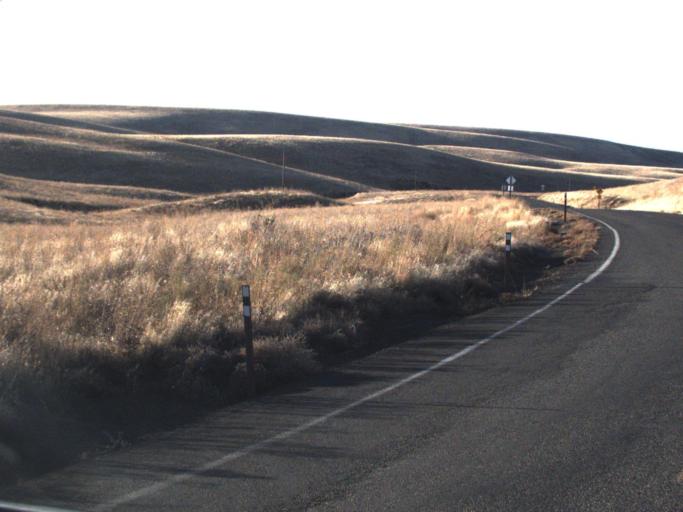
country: US
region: Washington
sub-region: Adams County
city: Ritzville
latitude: 46.6809
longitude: -118.3794
